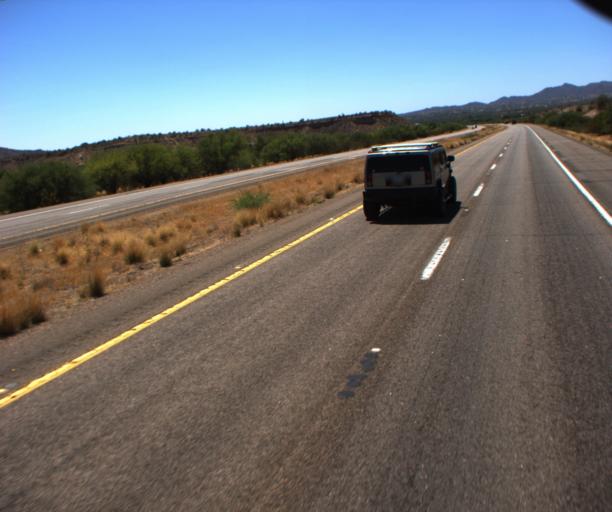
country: US
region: Arizona
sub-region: Maricopa County
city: Fountain Hills
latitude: 33.5817
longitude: -111.6489
